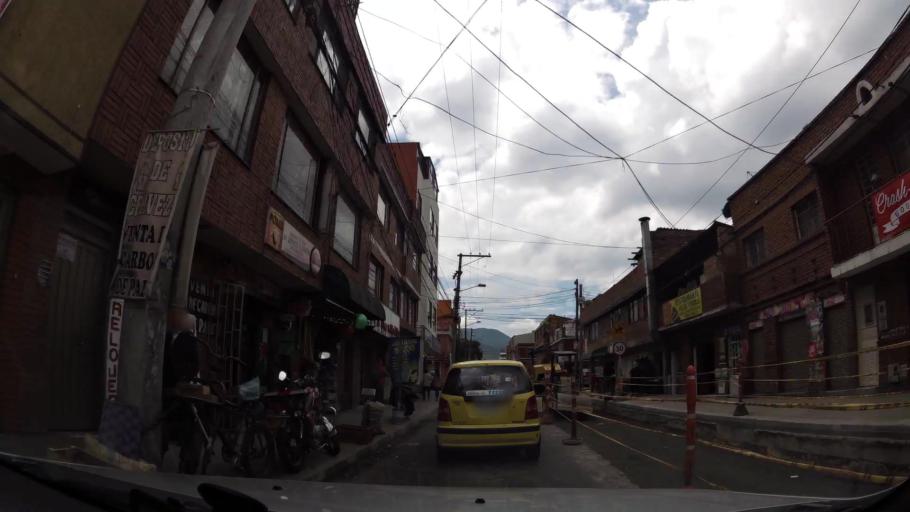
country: CO
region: Bogota D.C.
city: Bogota
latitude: 4.6024
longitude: -74.1059
